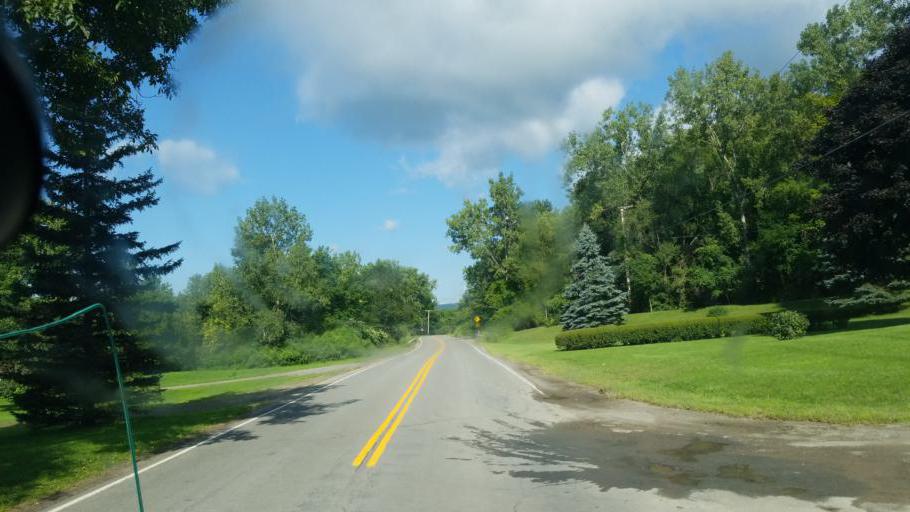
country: US
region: New York
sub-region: Steuben County
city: Canisteo
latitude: 42.2860
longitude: -77.6075
